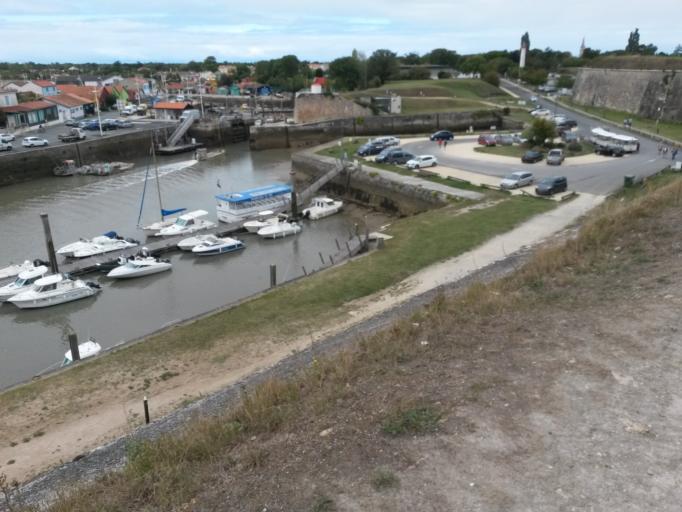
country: FR
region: Poitou-Charentes
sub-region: Departement de la Charente-Maritime
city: Saint-Trojan-les-Bains
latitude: 45.8835
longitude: -1.1892
